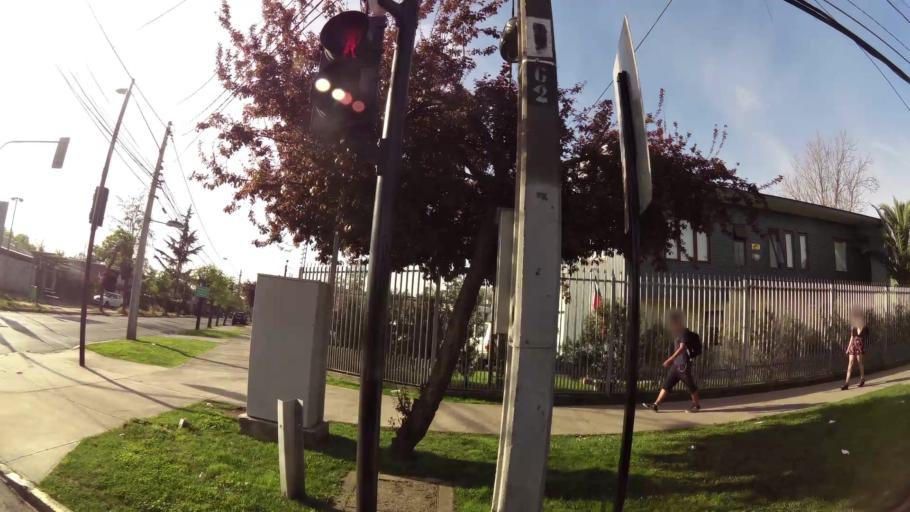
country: CL
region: Santiago Metropolitan
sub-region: Provincia de Santiago
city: La Pintana
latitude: -33.5358
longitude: -70.5874
